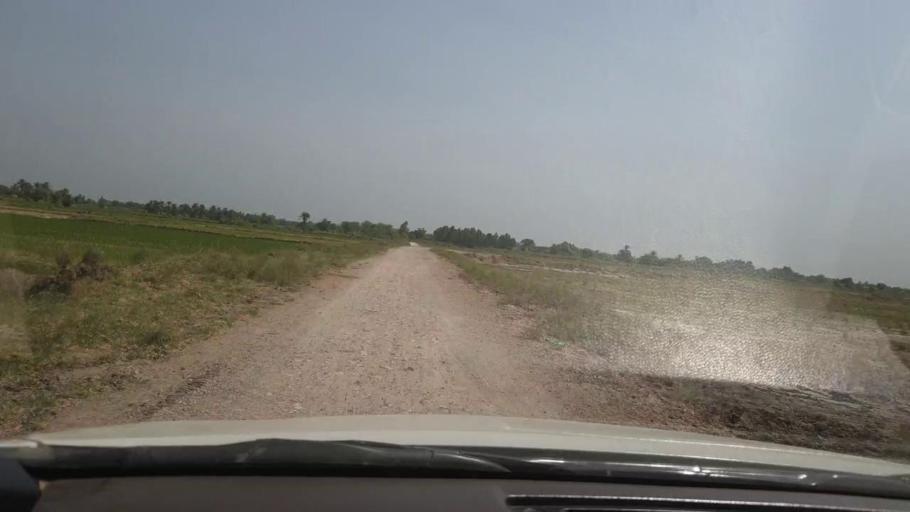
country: PK
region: Sindh
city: Shikarpur
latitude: 27.9227
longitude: 68.6059
